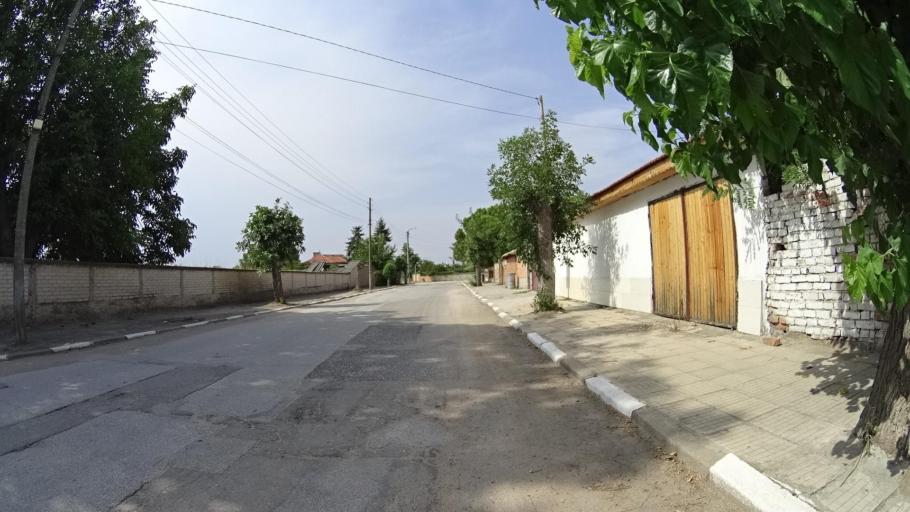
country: BG
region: Plovdiv
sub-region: Obshtina Kaloyanovo
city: Kaloyanovo
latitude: 42.2655
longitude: 24.8000
